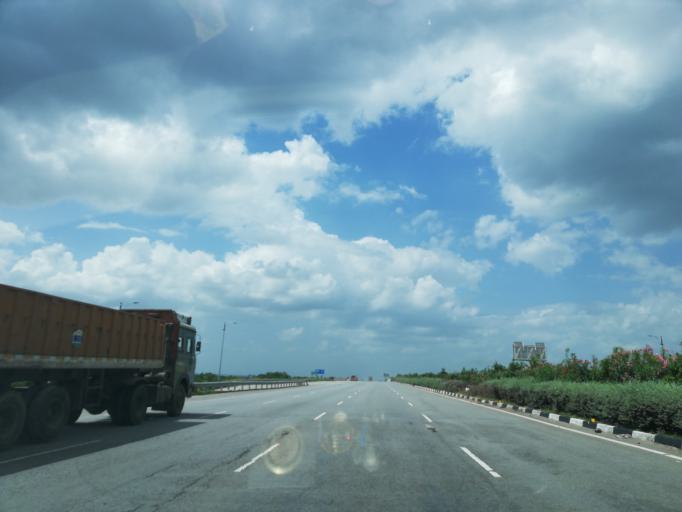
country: IN
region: Telangana
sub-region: Medak
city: Serilingampalle
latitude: 17.4657
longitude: 78.2491
